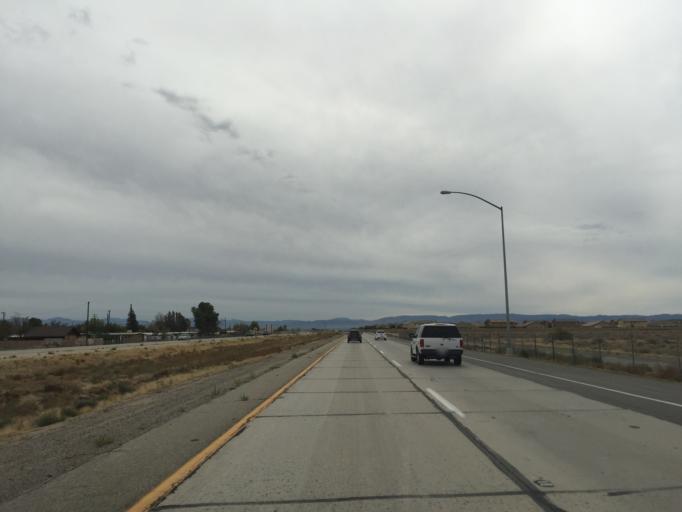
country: US
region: California
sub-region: Kern County
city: Rosamond
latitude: 34.8603
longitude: -118.1721
